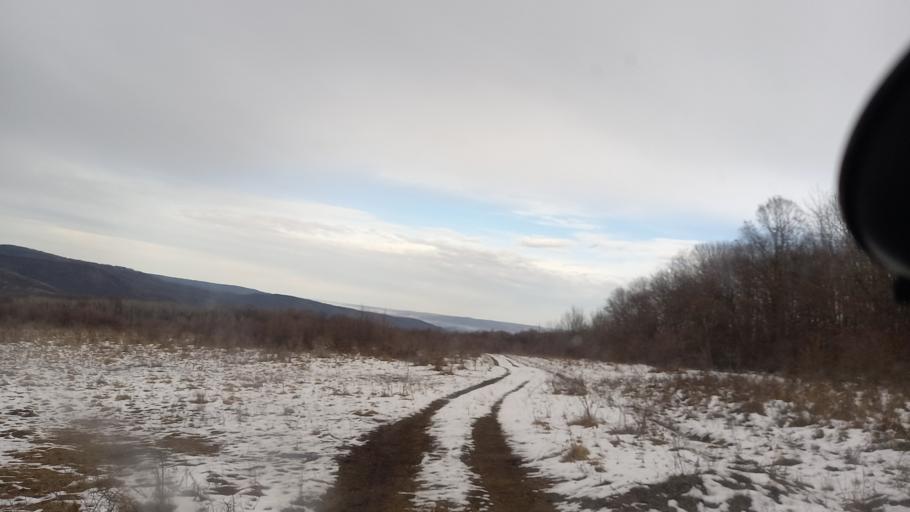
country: RU
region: Adygeya
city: Kamennomostskiy
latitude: 44.2507
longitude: 40.1788
